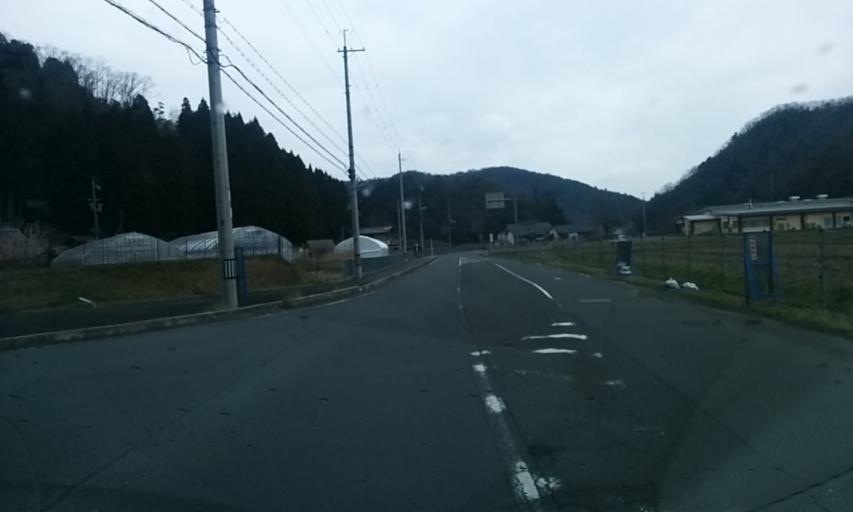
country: JP
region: Hyogo
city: Sasayama
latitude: 35.1317
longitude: 135.4123
